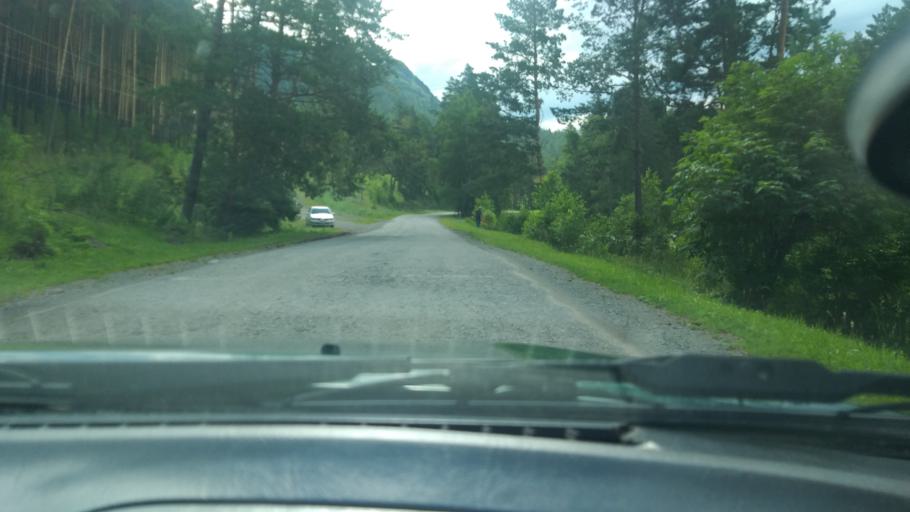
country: RU
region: Altay
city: Chemal
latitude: 51.3912
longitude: 86.0477
